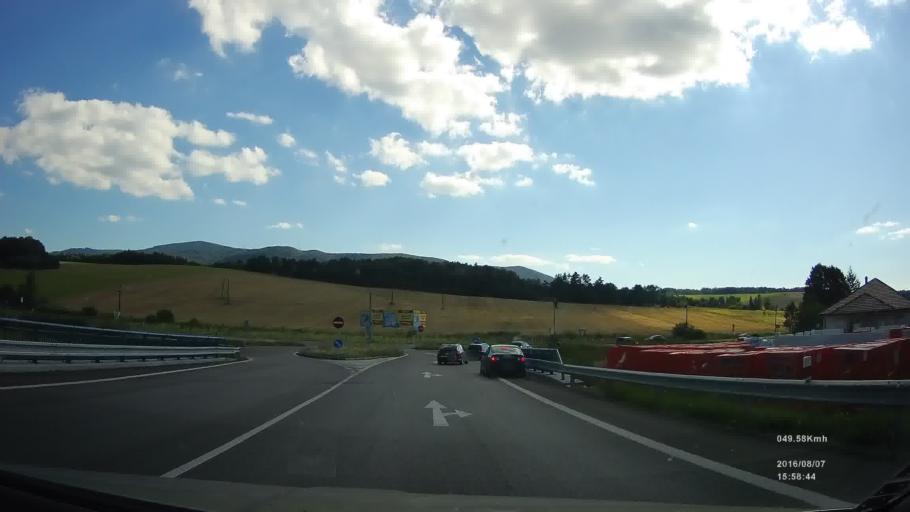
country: SK
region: Presovsky
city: Giraltovce
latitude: 49.0470
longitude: 21.4148
